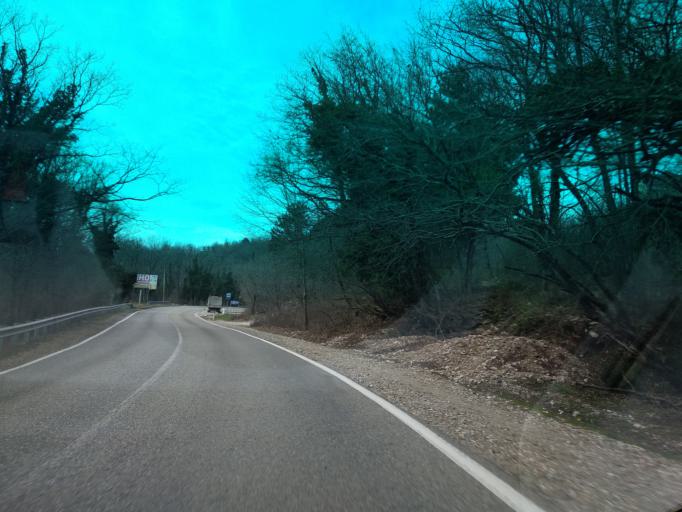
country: RU
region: Krasnodarskiy
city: Shepsi
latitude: 44.0748
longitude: 39.1357
